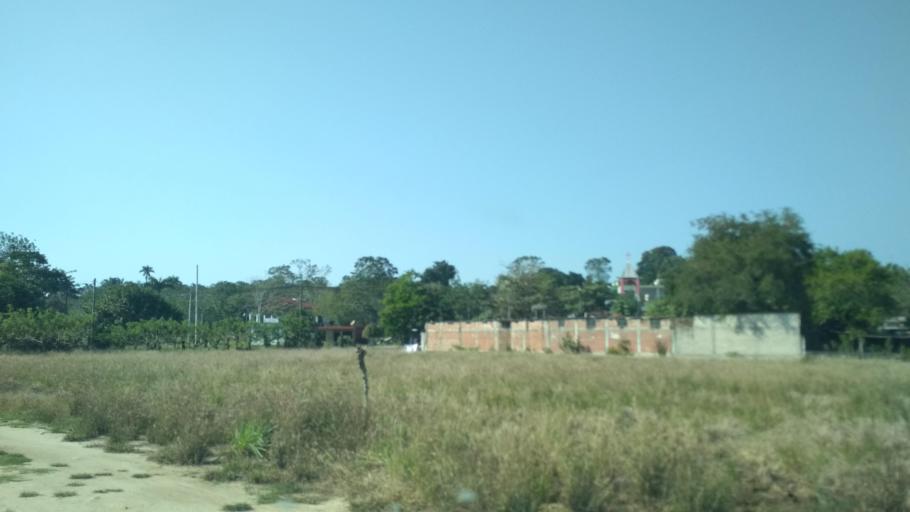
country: MX
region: Veracruz
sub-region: Martinez de la Torre
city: El Progreso
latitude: 20.0868
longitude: -97.0218
